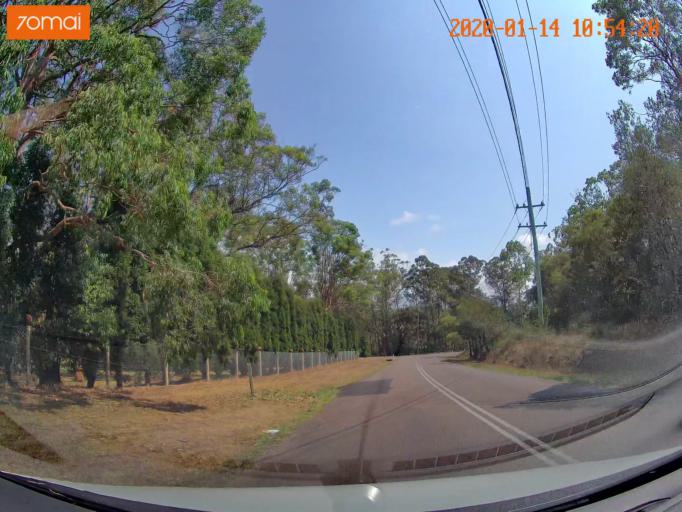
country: AU
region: New South Wales
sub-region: Lake Macquarie Shire
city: Dora Creek
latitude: -33.0988
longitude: 151.4870
